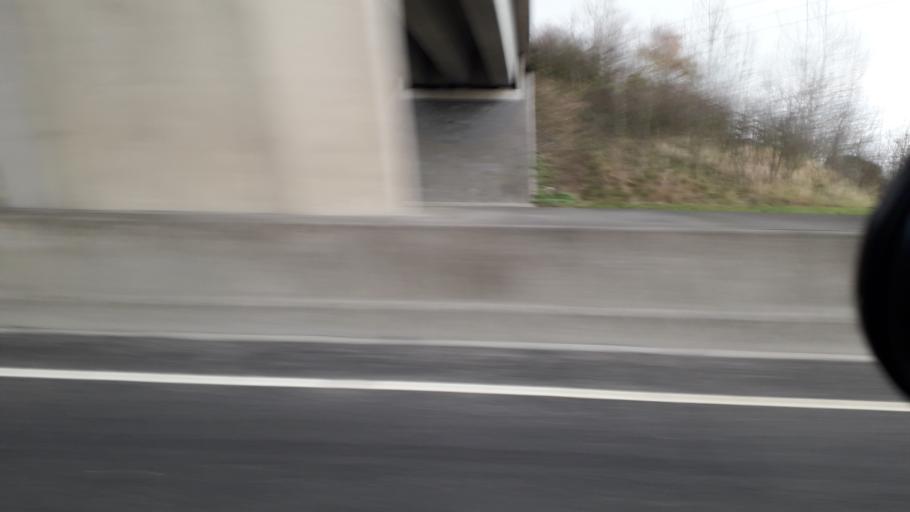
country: IE
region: Leinster
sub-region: An Mhi
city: Ashbourne
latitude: 53.4852
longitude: -6.3798
